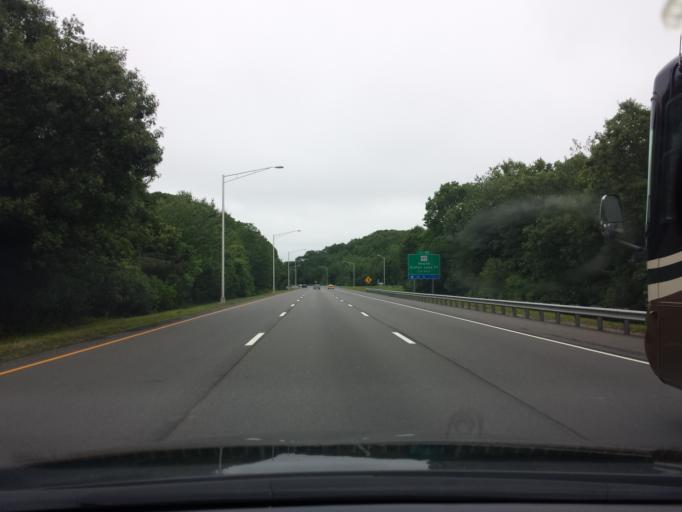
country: US
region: Connecticut
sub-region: New London County
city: Long Hill
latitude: 41.3607
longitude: -72.0556
